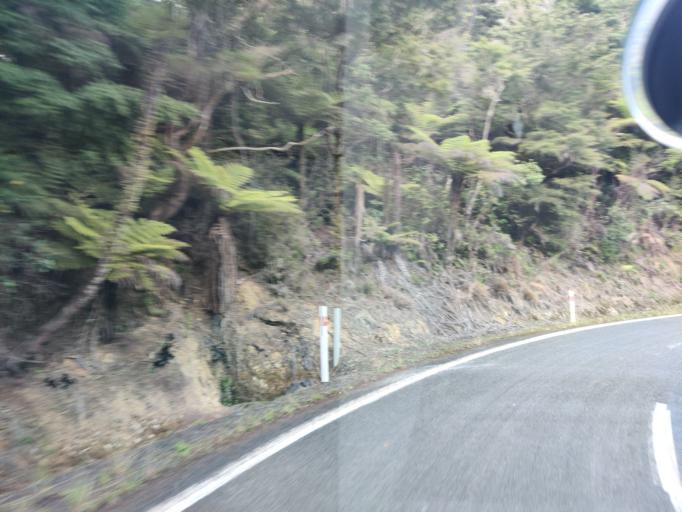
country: NZ
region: Northland
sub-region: Whangarei
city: Ngunguru
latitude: -35.5786
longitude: 174.4047
